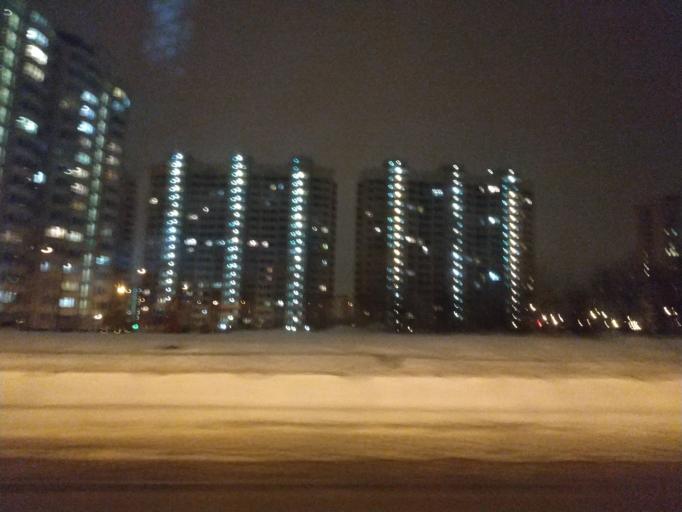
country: RU
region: Moscow
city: Nekrasovka
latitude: 55.7069
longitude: 37.9337
